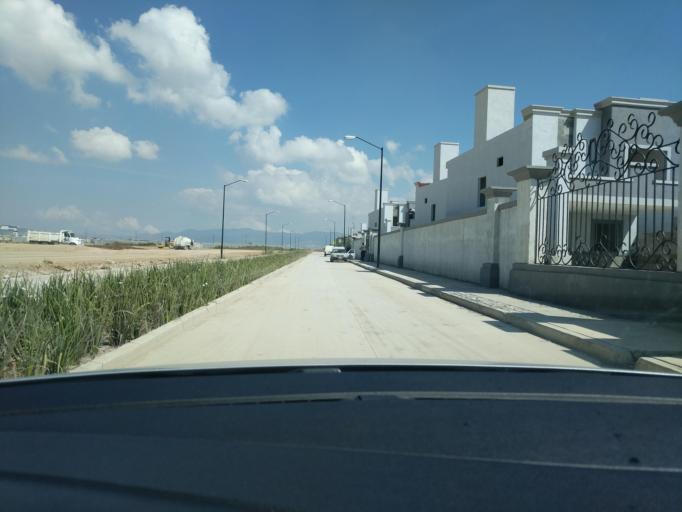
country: MX
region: Hidalgo
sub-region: Zempoala
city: Jagueey de Tellez (Estacion Tellez)
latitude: 20.0042
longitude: -98.7743
